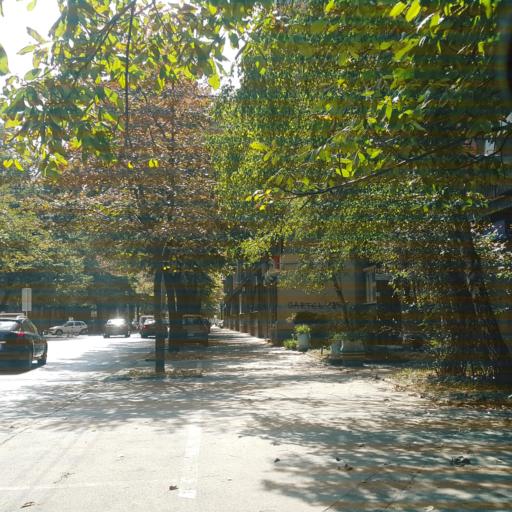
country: RS
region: Central Serbia
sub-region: Nisavski Okrug
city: Nis
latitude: 43.3192
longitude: 21.8877
